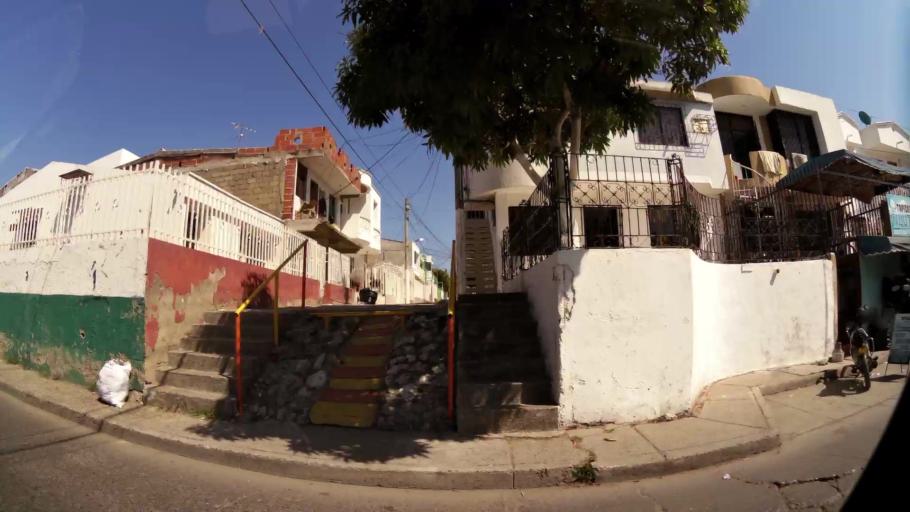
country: CO
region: Bolivar
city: Cartagena
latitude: 10.3890
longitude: -75.5092
